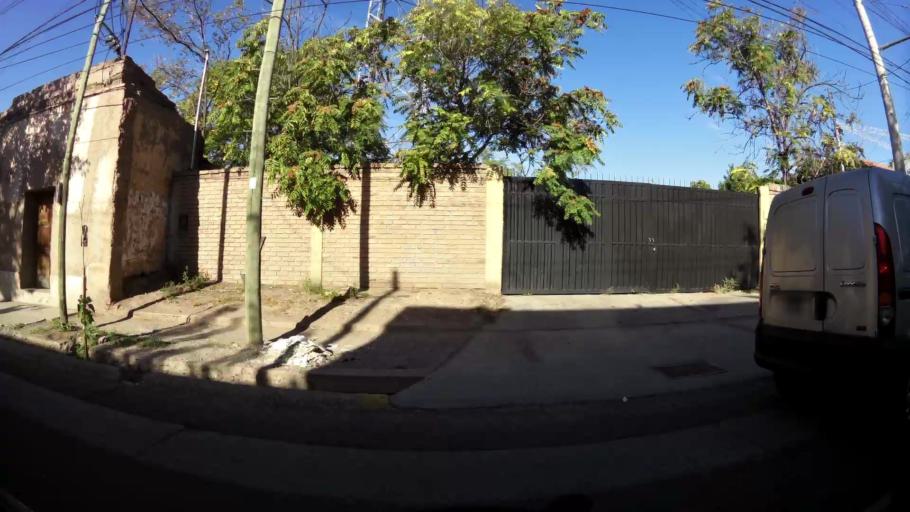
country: AR
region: Mendoza
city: Mendoza
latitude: -32.9049
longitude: -68.8287
